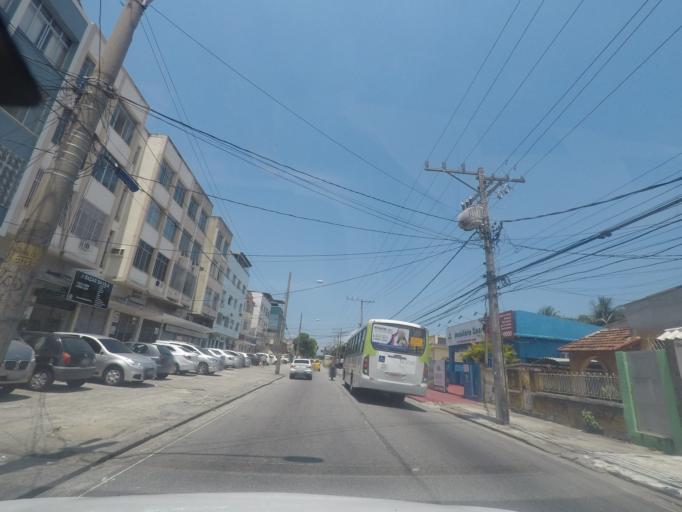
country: BR
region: Rio de Janeiro
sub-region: Duque De Caxias
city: Duque de Caxias
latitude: -22.8403
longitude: -43.3007
